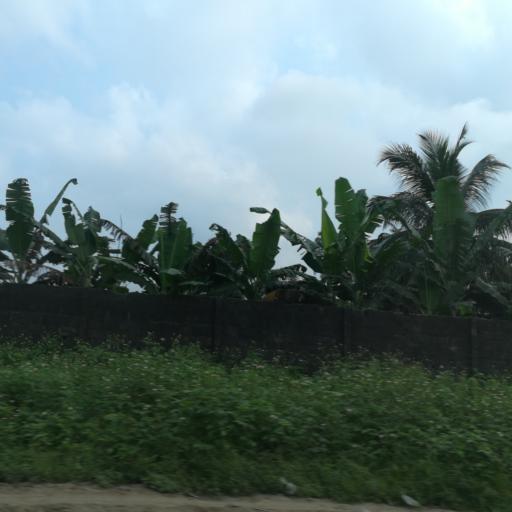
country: NG
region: Rivers
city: Okrika
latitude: 4.7725
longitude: 7.1369
